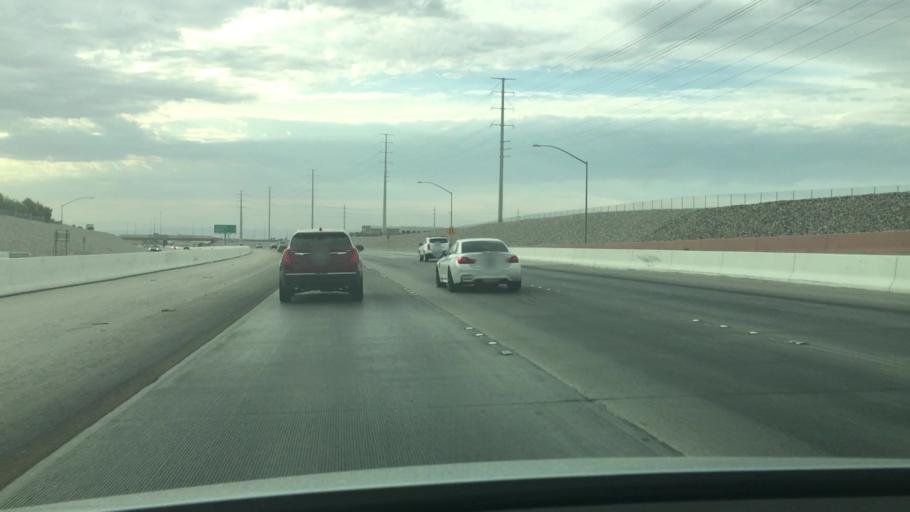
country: US
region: Nevada
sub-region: Clark County
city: Summerlin South
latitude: 36.1204
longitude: -115.3238
